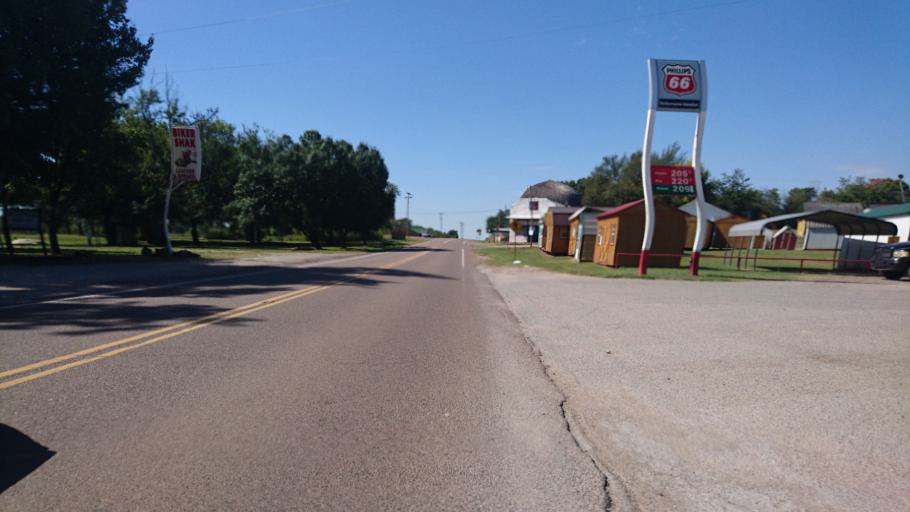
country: US
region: Oklahoma
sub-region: Oklahoma County
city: Jones
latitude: 35.6628
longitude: -97.3244
